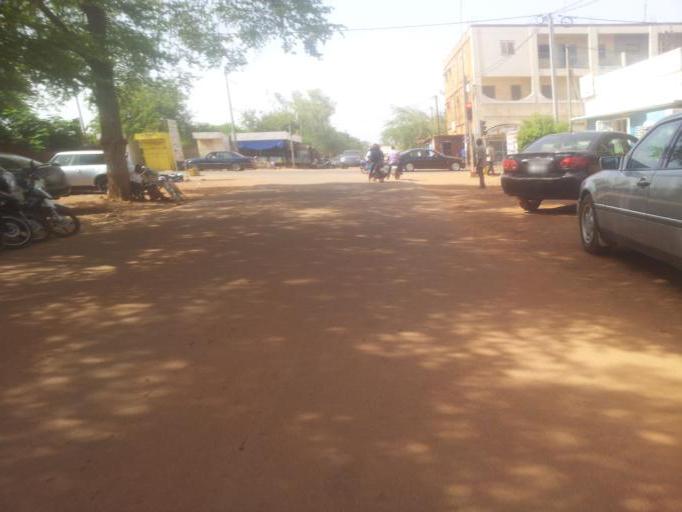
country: BF
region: Centre
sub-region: Kadiogo Province
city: Ouagadougou
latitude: 12.3771
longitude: -1.5368
